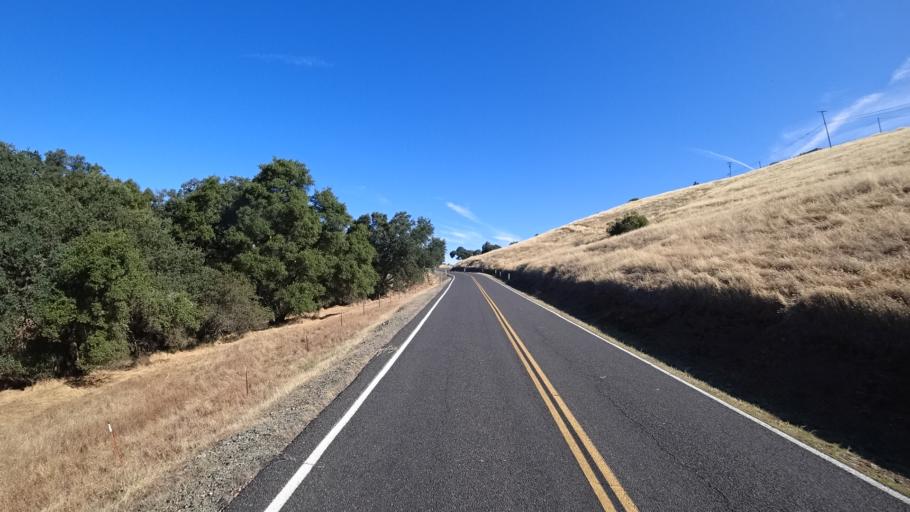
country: US
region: California
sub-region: Calaveras County
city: Valley Springs
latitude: 38.1528
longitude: -120.8156
